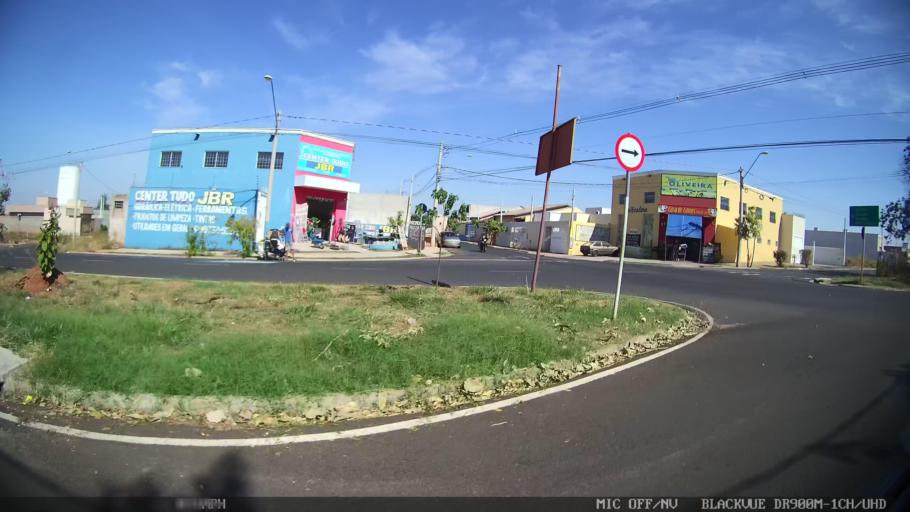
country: BR
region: Sao Paulo
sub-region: Sao Jose Do Rio Preto
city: Sao Jose do Rio Preto
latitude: -20.7805
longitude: -49.4200
